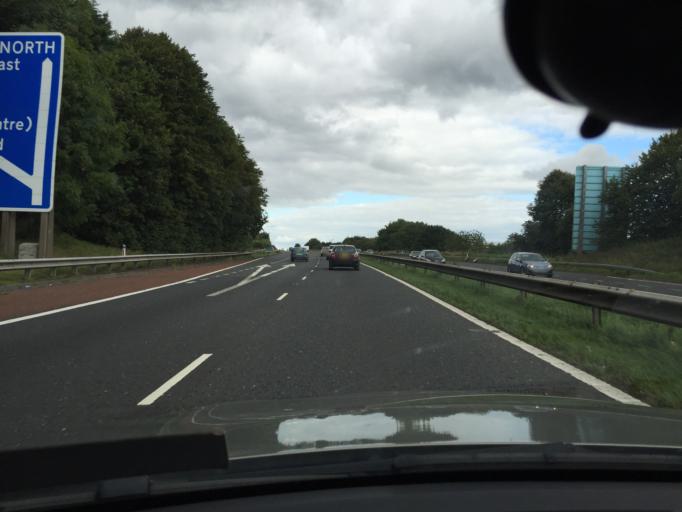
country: GB
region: Northern Ireland
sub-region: Lisburn District
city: Lisburn
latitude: 54.5020
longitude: -6.0339
